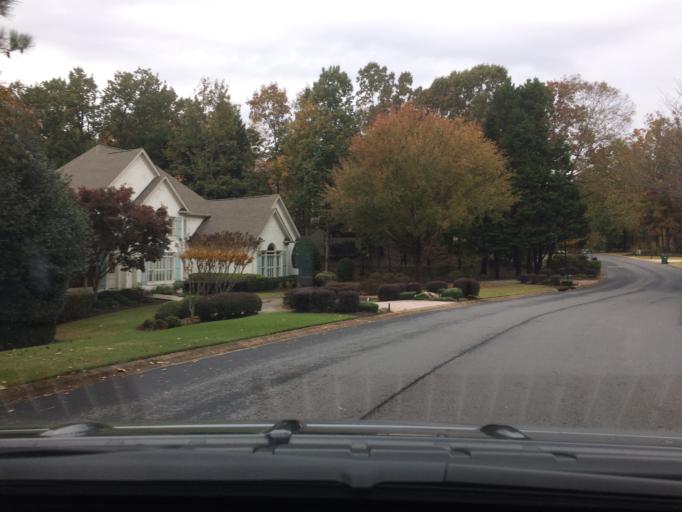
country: US
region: Georgia
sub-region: Fulton County
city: Johns Creek
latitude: 34.0045
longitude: -84.2509
